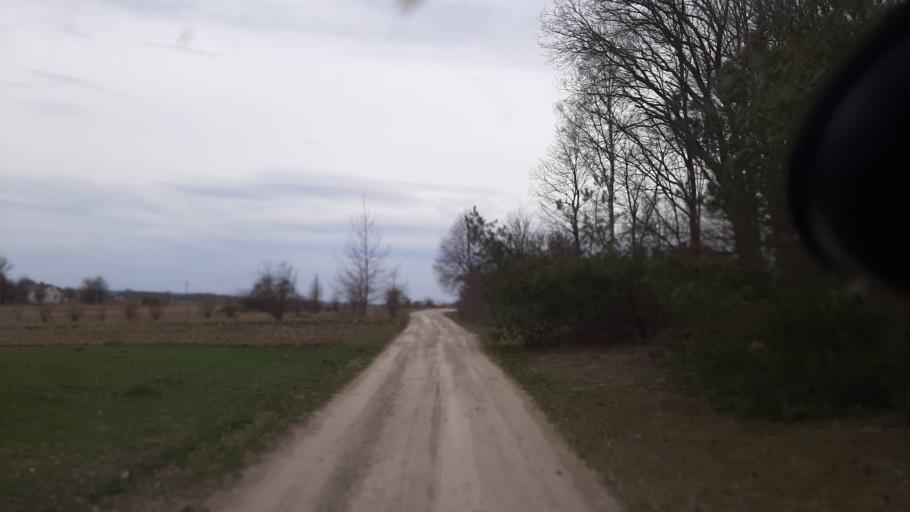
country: PL
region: Lublin Voivodeship
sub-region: Powiat lubartowski
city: Abramow
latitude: 51.4459
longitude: 22.3369
